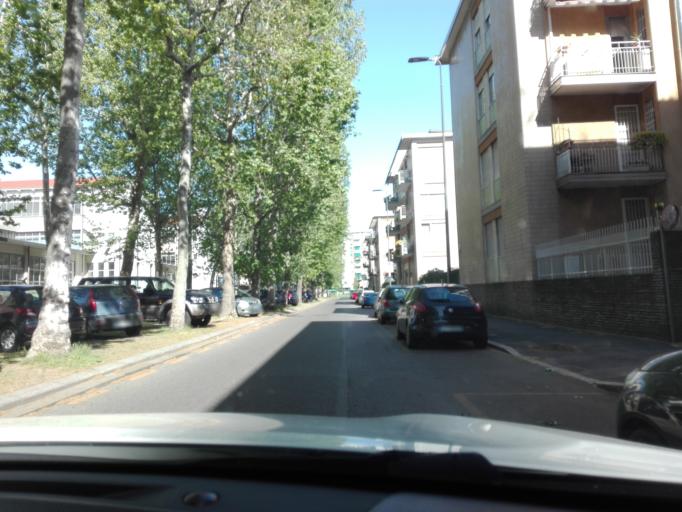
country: IT
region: Lombardy
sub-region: Citta metropolitana di Milano
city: Romano Banco
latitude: 45.4759
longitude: 9.1403
